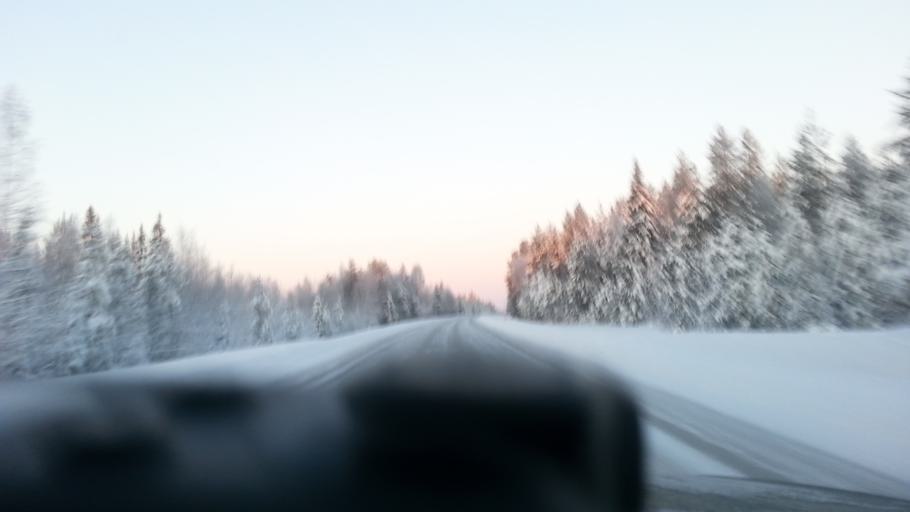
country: FI
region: Lapland
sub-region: Tunturi-Lappi
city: Kittilae
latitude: 67.2172
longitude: 24.9245
